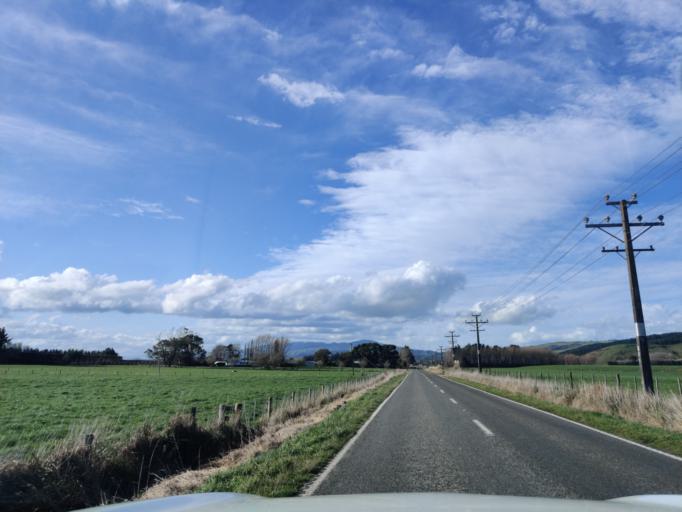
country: NZ
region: Manawatu-Wanganui
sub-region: Palmerston North City
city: Palmerston North
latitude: -40.3418
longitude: 175.7157
